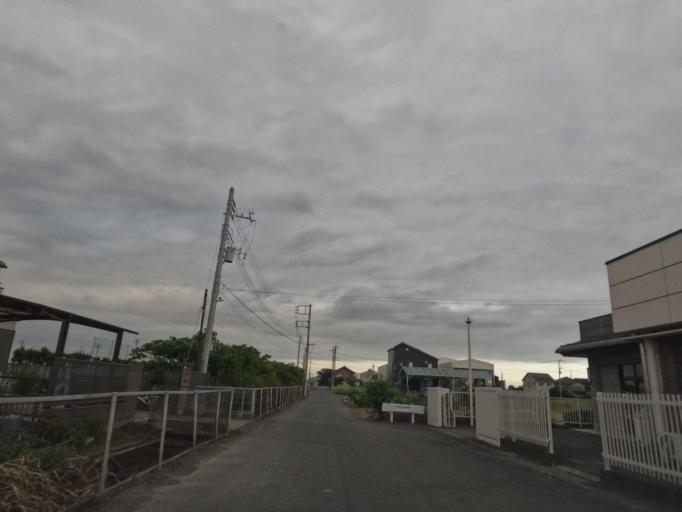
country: JP
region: Saitama
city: Koshigaya
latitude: 35.9032
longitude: 139.7598
